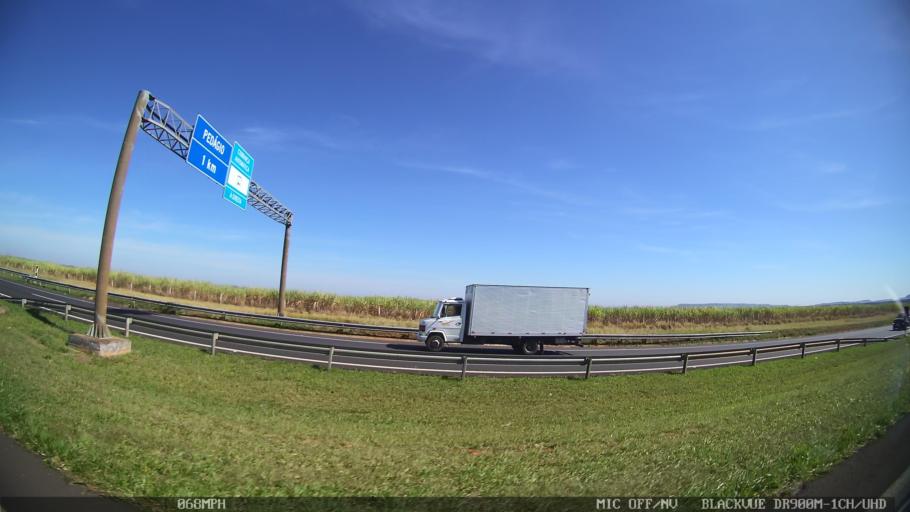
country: BR
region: Sao Paulo
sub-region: Santa Rita Do Passa Quatro
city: Santa Rita do Passa Quatro
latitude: -21.6495
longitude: -47.6105
